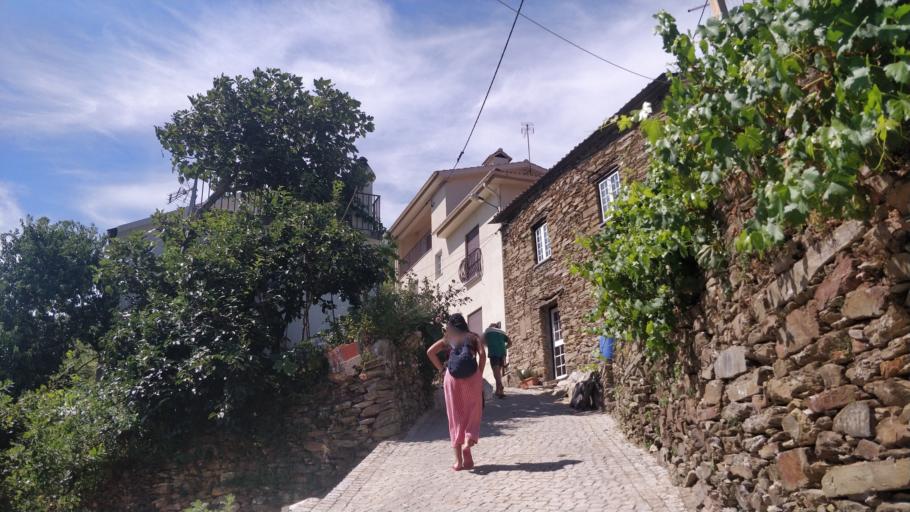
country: PT
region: Guarda
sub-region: Seia
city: Seia
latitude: 40.2857
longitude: -7.7214
